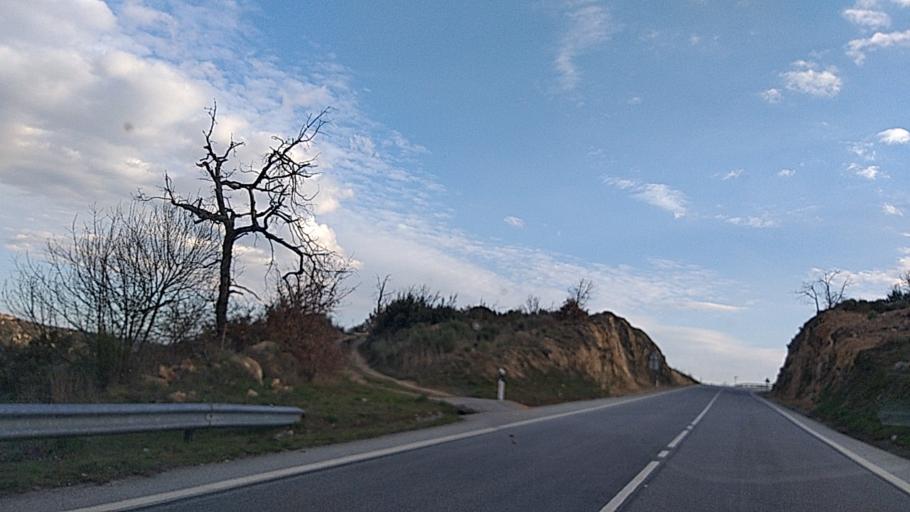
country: ES
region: Castille and Leon
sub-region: Provincia de Salamanca
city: Aldea del Obispo
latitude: 40.6998
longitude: -6.9336
